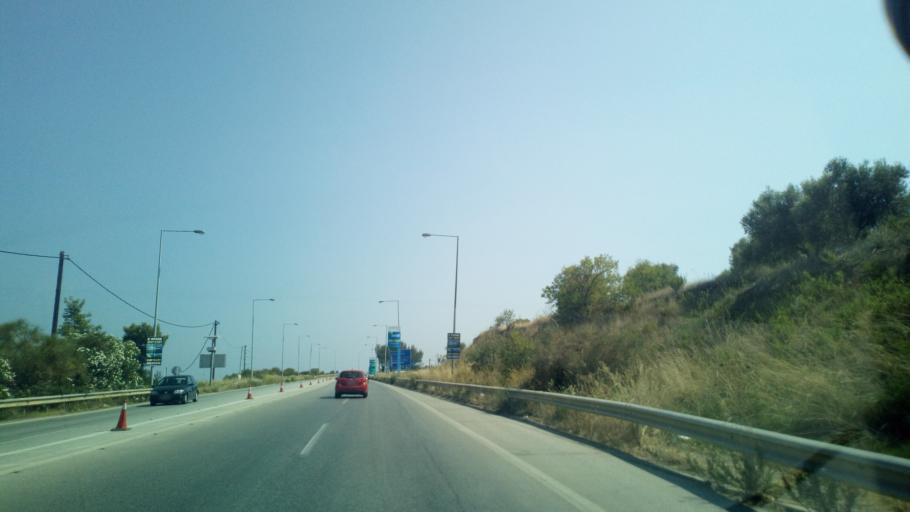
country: GR
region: Central Macedonia
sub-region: Nomos Chalkidikis
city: Nea Potidhaia
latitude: 40.2009
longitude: 23.3275
